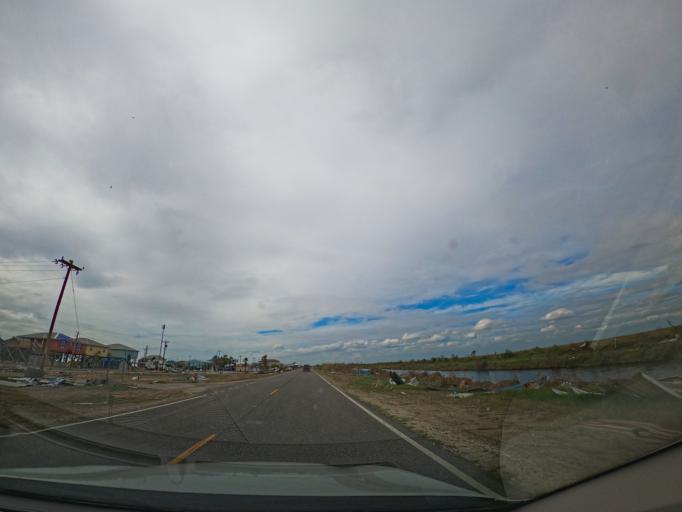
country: US
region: Louisiana
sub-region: Cameron Parish
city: Cameron
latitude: 29.7720
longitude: -93.4512
